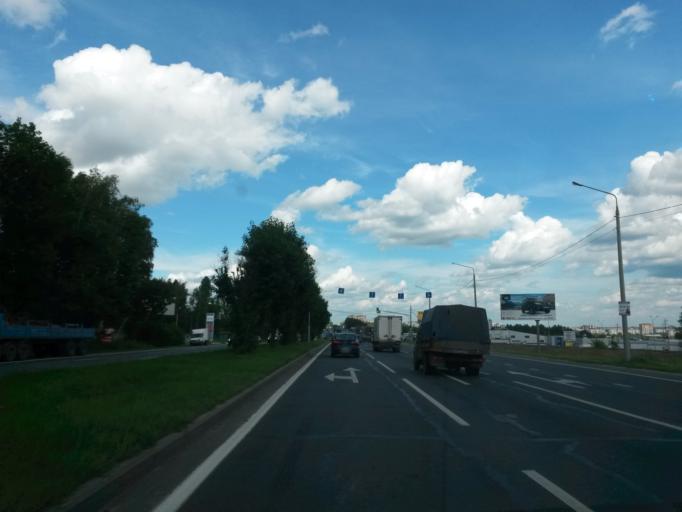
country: RU
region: Jaroslavl
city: Yaroslavl
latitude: 57.5599
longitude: 39.8226
